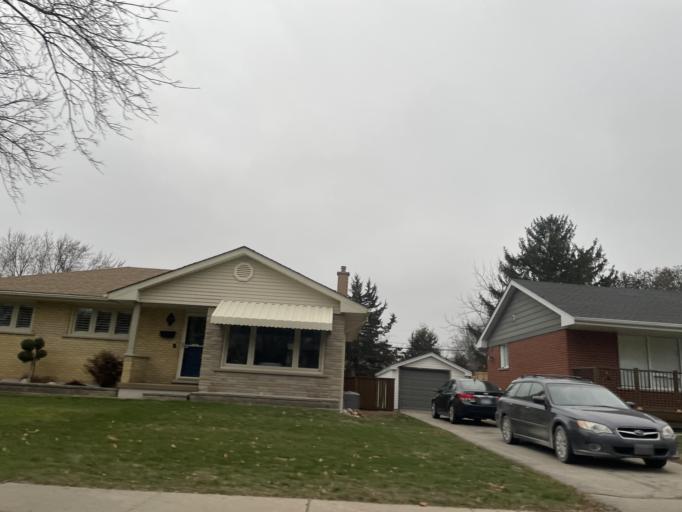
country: CA
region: Ontario
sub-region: Wellington County
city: Guelph
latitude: 43.5410
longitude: -80.2712
